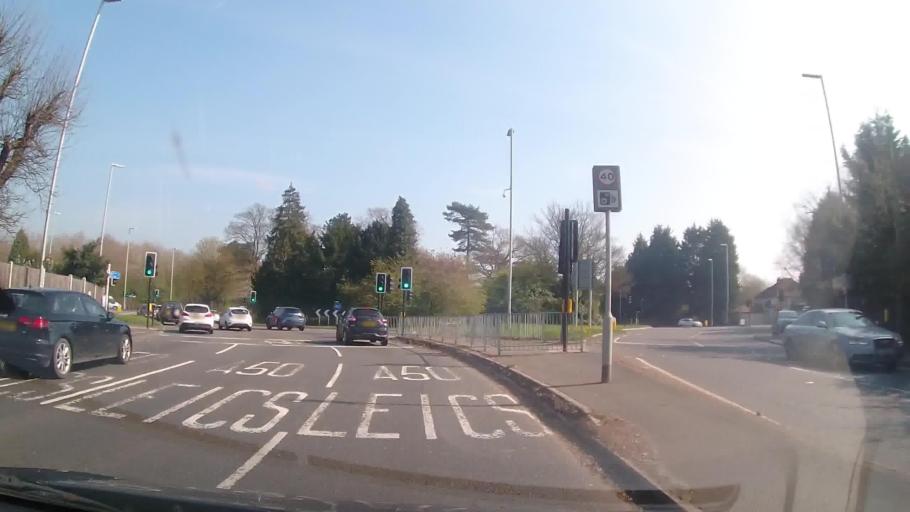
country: GB
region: England
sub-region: Leicestershire
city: Glenfield
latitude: 52.6577
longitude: -1.1962
